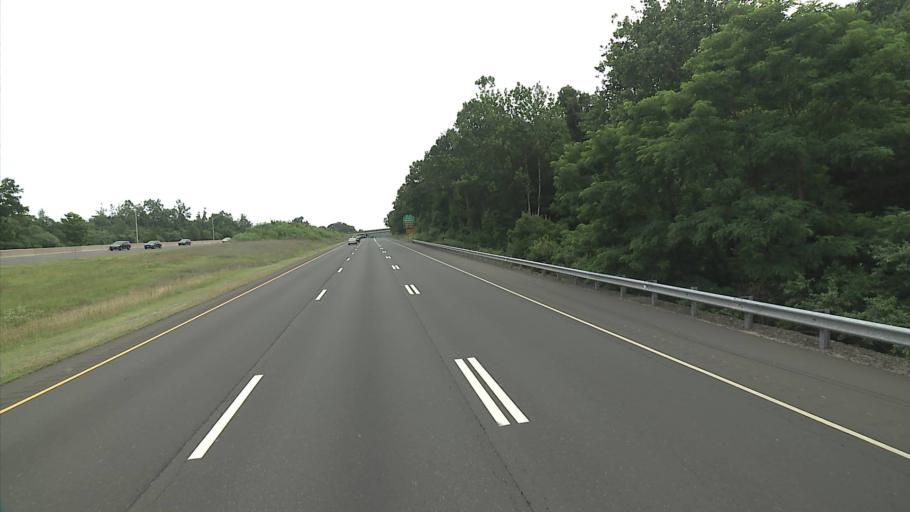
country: US
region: Connecticut
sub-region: New Haven County
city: Southbury
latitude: 41.4693
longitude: -73.2191
